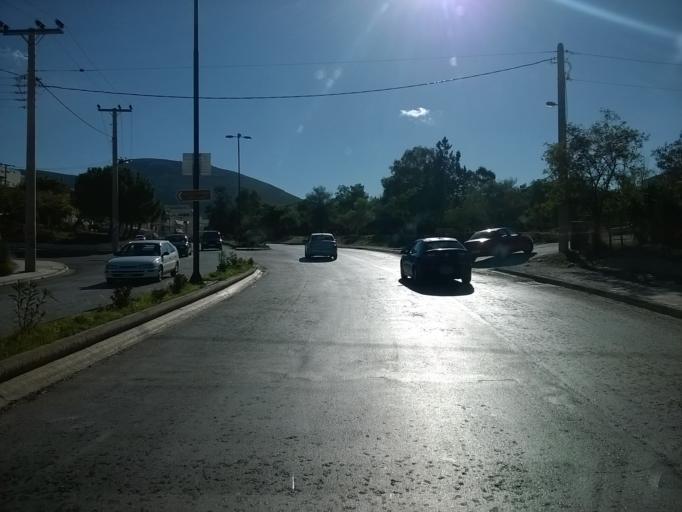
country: GR
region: Attica
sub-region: Nomarchia Athinas
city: Argyroupoli
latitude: 37.8965
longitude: 23.7595
